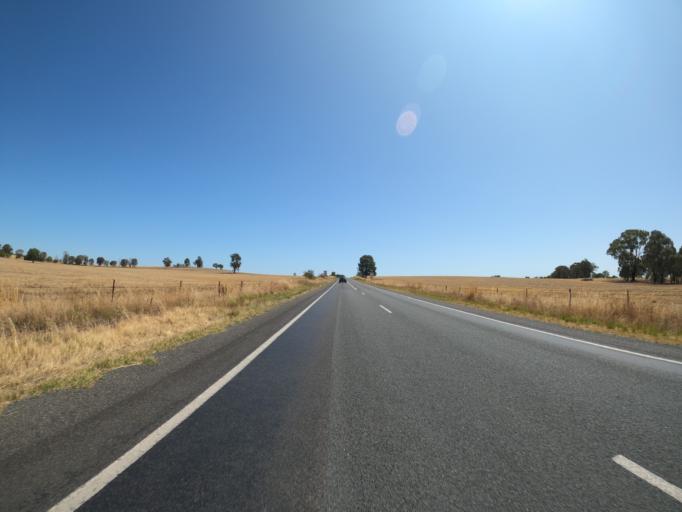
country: AU
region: New South Wales
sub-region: Corowa Shire
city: Corowa
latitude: -36.0552
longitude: 146.4440
